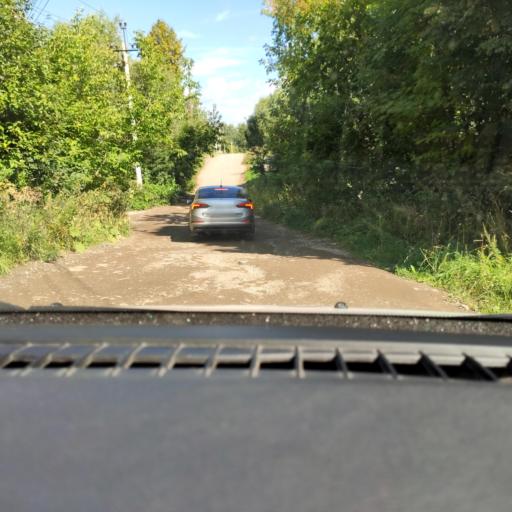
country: RU
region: Perm
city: Perm
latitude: 58.1132
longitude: 56.3895
